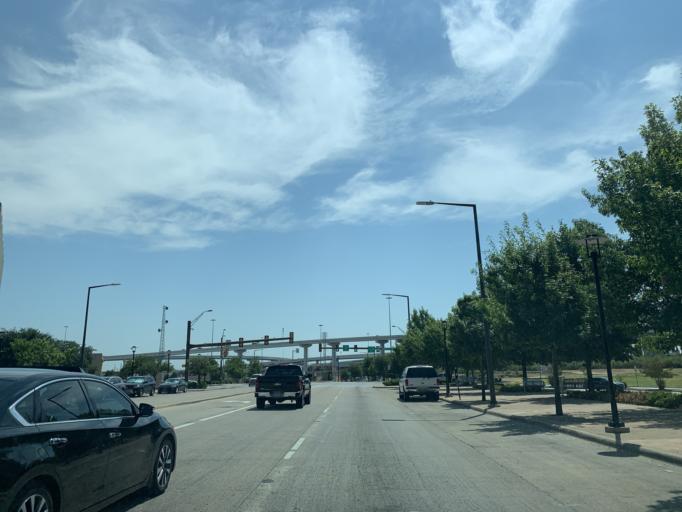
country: US
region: Texas
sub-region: Tarrant County
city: Fort Worth
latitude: 32.7465
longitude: -97.3260
